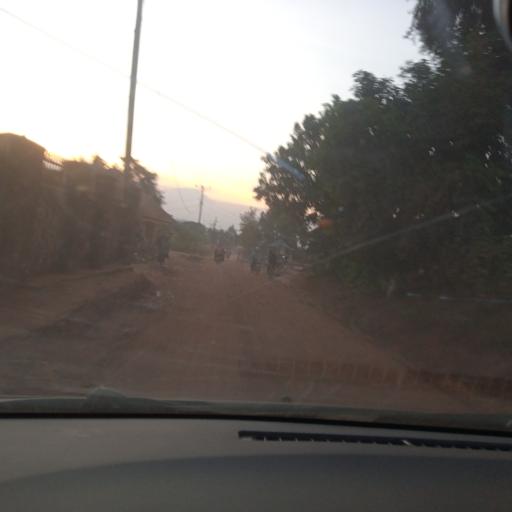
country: UG
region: Central Region
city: Masaka
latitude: -0.3108
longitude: 31.7649
